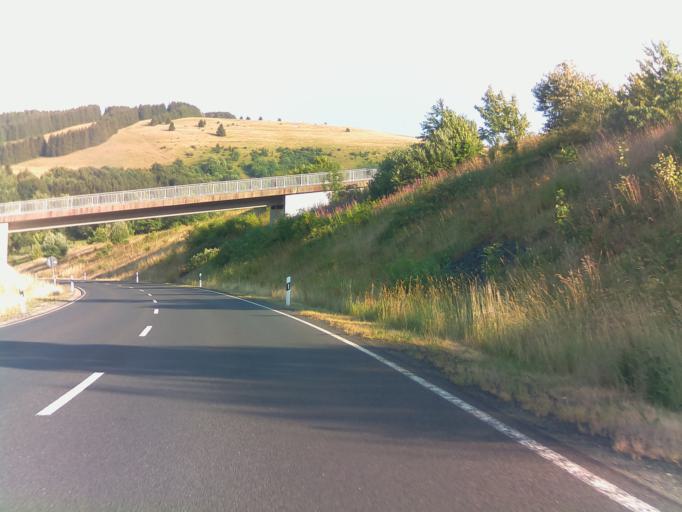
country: DE
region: Bavaria
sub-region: Regierungsbezirk Unterfranken
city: Wildflecken
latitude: 50.4068
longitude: 9.9481
